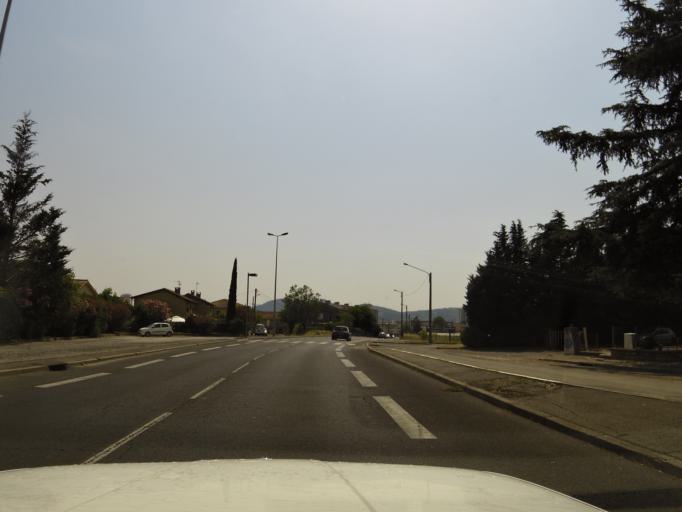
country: FR
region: Languedoc-Roussillon
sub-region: Departement du Gard
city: Ales
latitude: 44.1444
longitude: 4.0952
